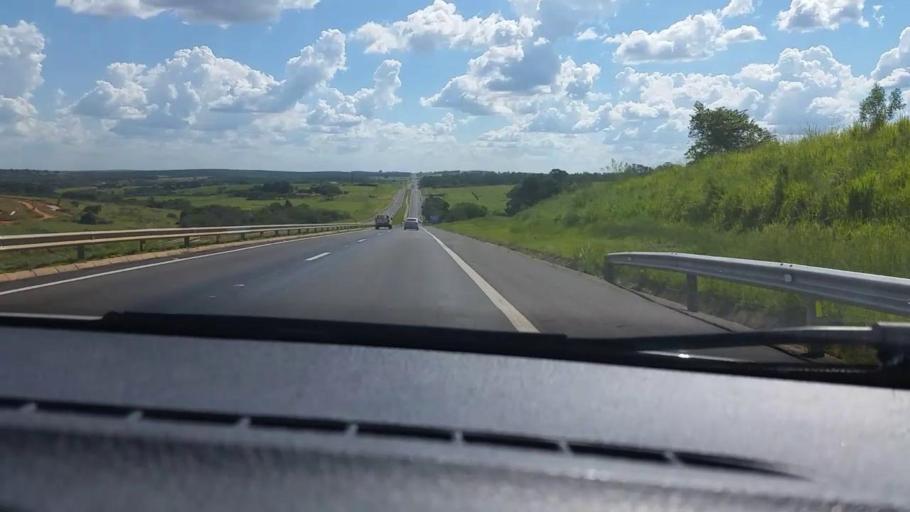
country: BR
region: Sao Paulo
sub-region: Bauru
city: Bauru
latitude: -22.4379
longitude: -49.1407
